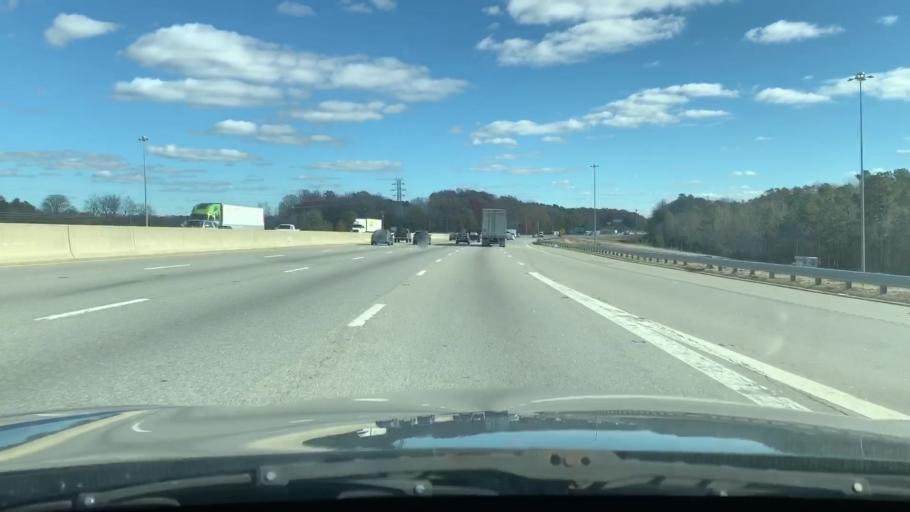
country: US
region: North Carolina
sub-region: Orange County
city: Hillsborough
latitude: 36.0729
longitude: -79.1611
